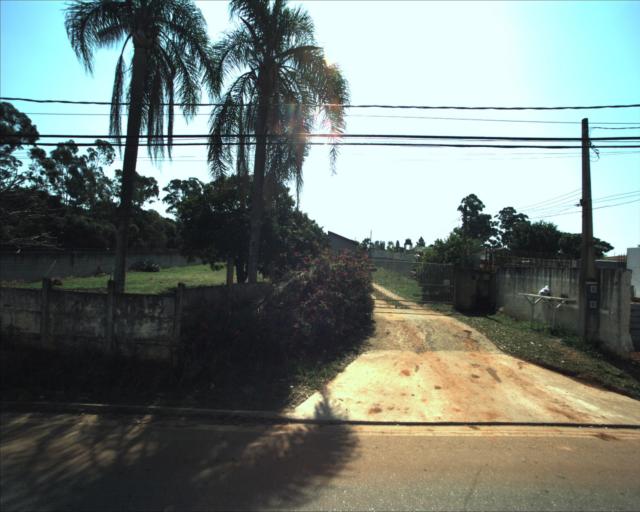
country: BR
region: Sao Paulo
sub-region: Sorocaba
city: Sorocaba
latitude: -23.4547
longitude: -47.4978
